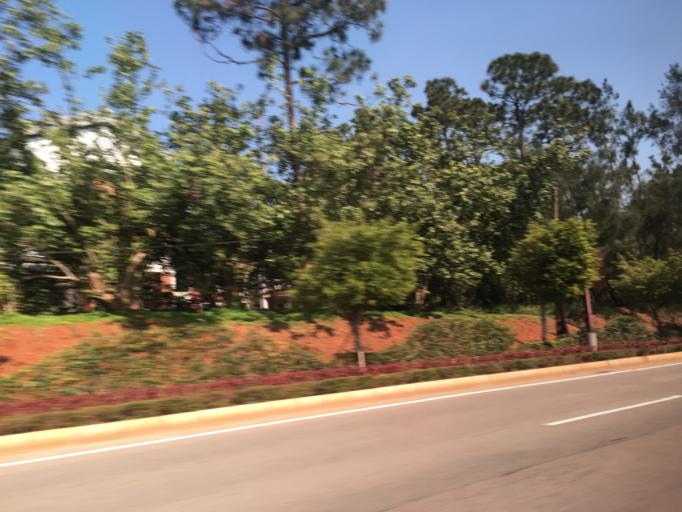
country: TW
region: Fukien
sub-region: Kinmen
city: Jincheng
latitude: 24.4363
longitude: 118.3534
